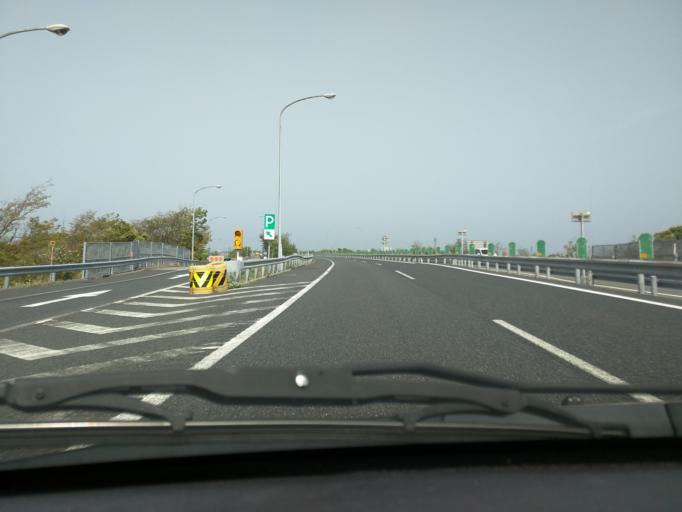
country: JP
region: Niigata
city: Kameda-honcho
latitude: 37.8468
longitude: 139.0628
